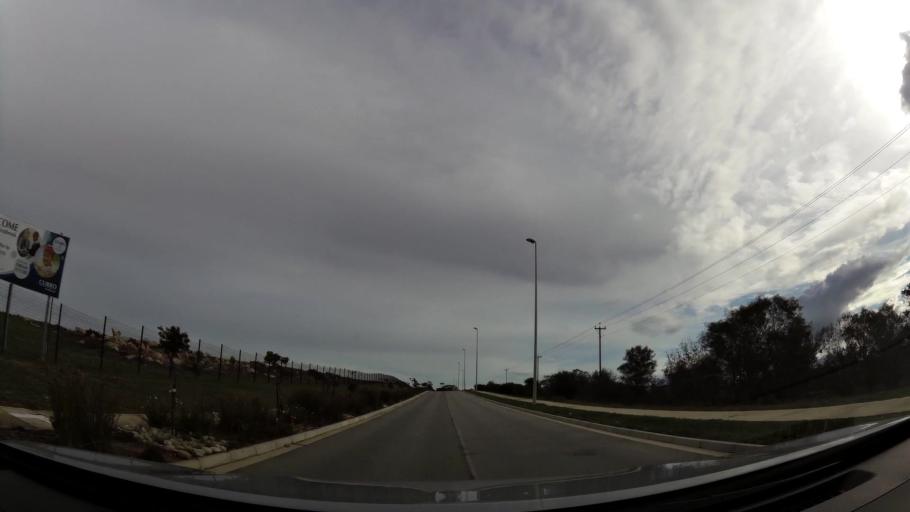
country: ZA
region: Eastern Cape
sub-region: Nelson Mandela Bay Metropolitan Municipality
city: Port Elizabeth
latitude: -33.9305
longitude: 25.4930
